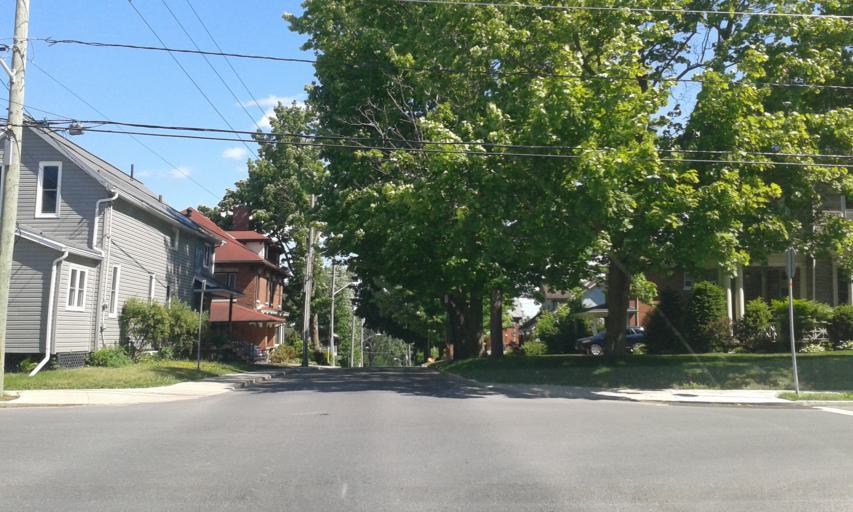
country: CA
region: Ontario
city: Brockville
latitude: 44.5952
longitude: -75.6809
